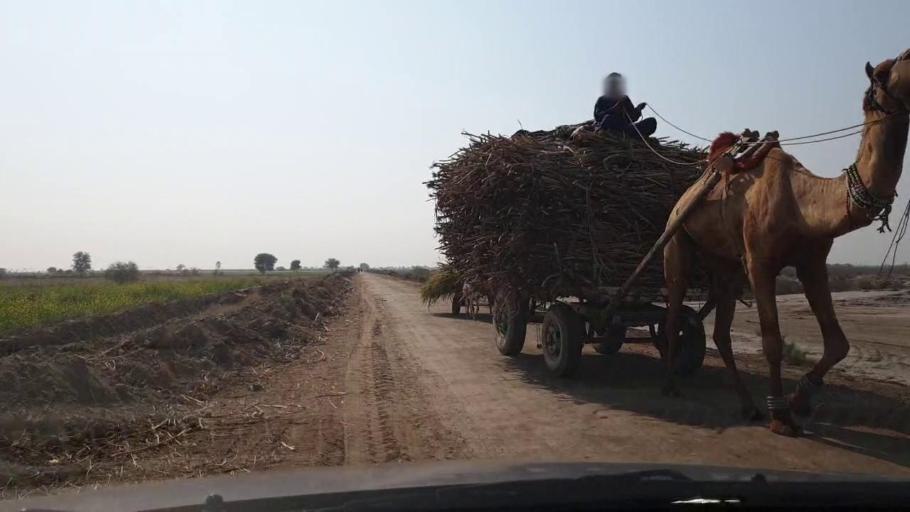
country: PK
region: Sindh
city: Jhol
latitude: 25.8581
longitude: 68.9932
